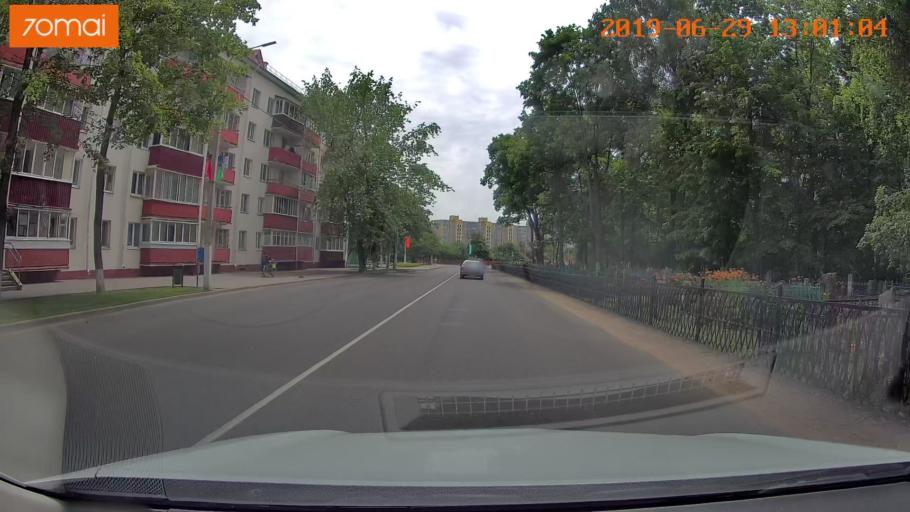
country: BY
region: Minsk
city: Slutsk
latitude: 53.0404
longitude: 27.5591
